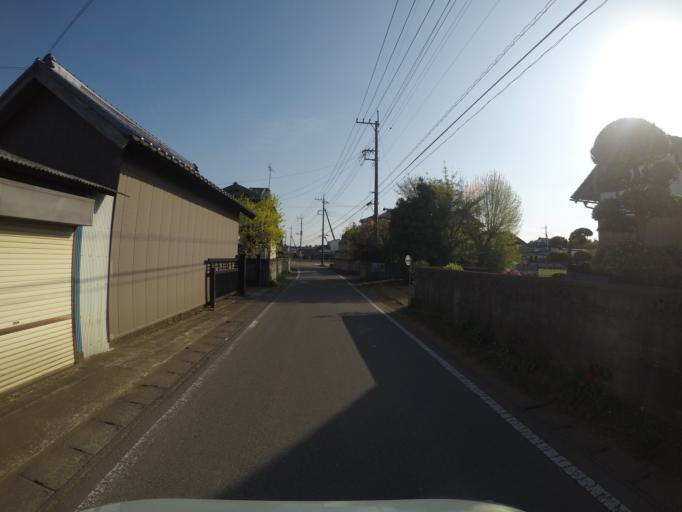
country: JP
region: Ibaraki
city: Ishige
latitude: 36.1641
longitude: 140.0151
